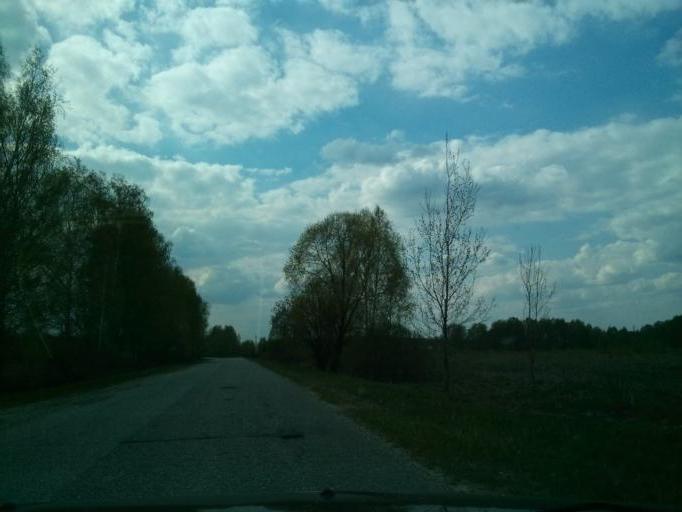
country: RU
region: Nizjnij Novgorod
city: Shimorskoye
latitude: 55.3399
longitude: 41.8700
